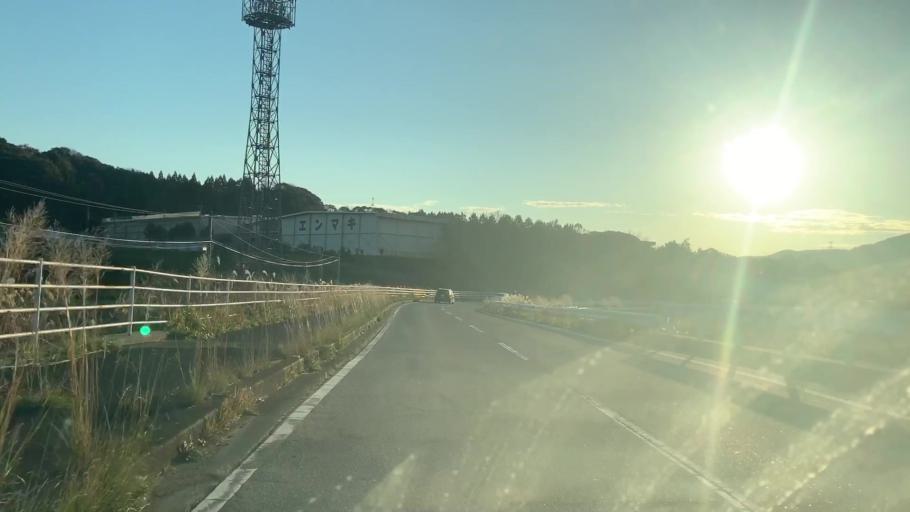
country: JP
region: Saga Prefecture
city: Karatsu
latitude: 33.3526
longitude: 130.0013
